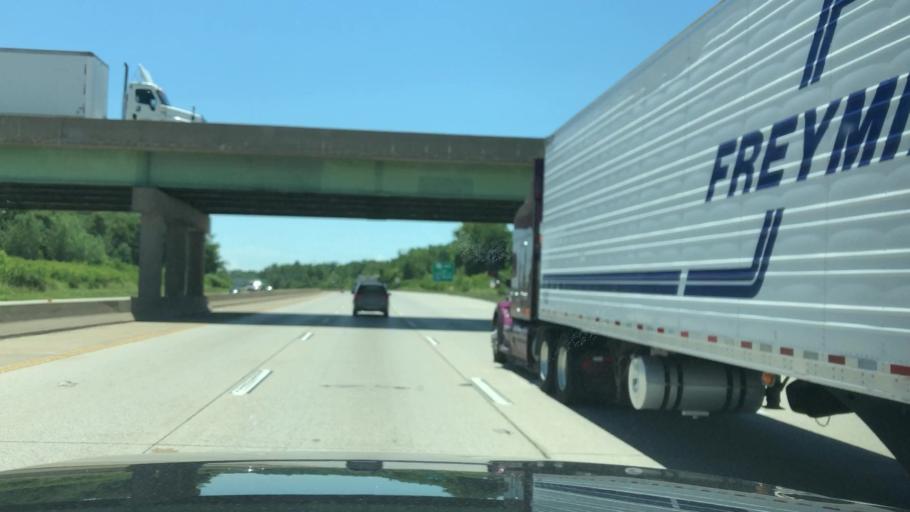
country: US
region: Missouri
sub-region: Saint Louis County
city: Bridgeton
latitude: 38.7810
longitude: -90.4170
